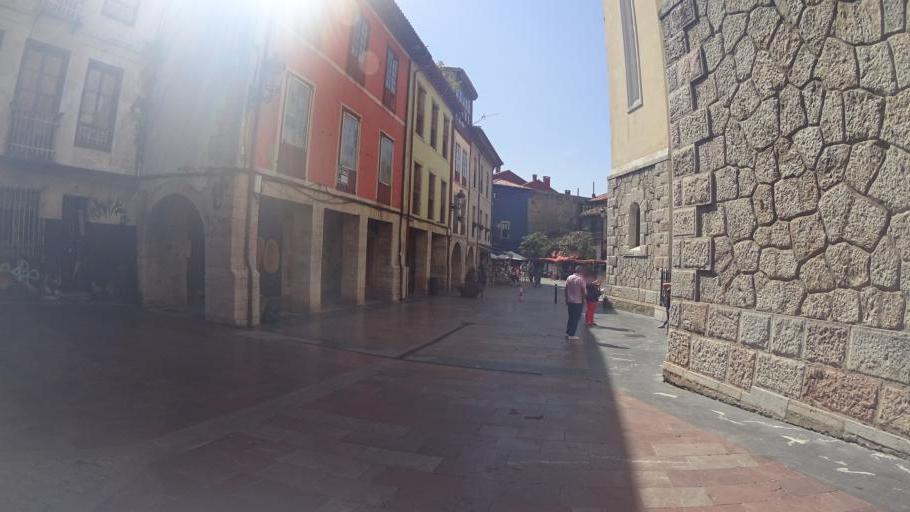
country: ES
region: Asturias
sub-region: Province of Asturias
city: Ribadesella
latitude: 43.4621
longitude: -5.0575
